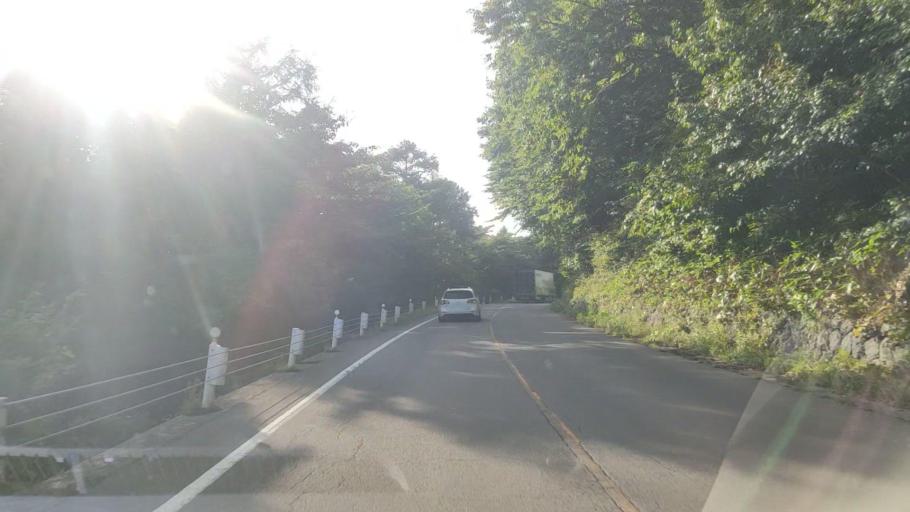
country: JP
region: Nagano
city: Ueda
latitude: 36.4895
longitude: 138.4053
